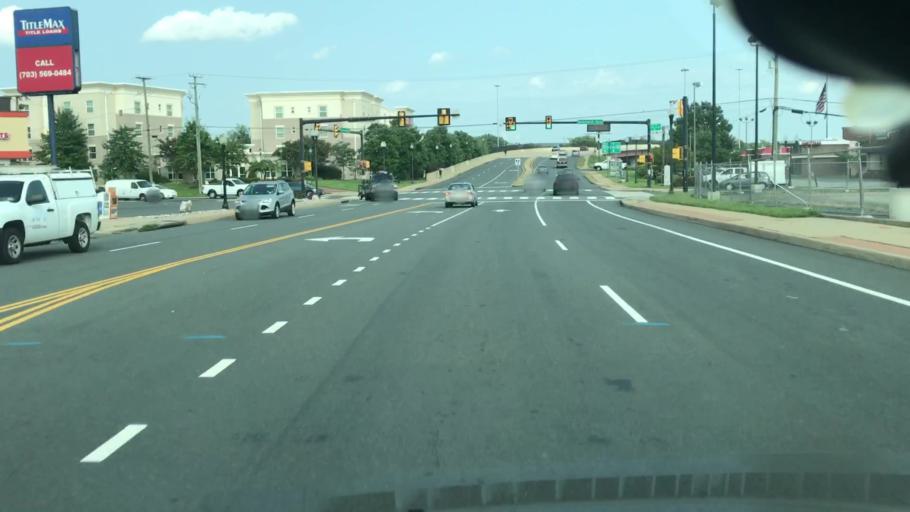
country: US
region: Virginia
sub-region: Fairfax County
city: Springfield
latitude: 38.7823
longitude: -77.1831
